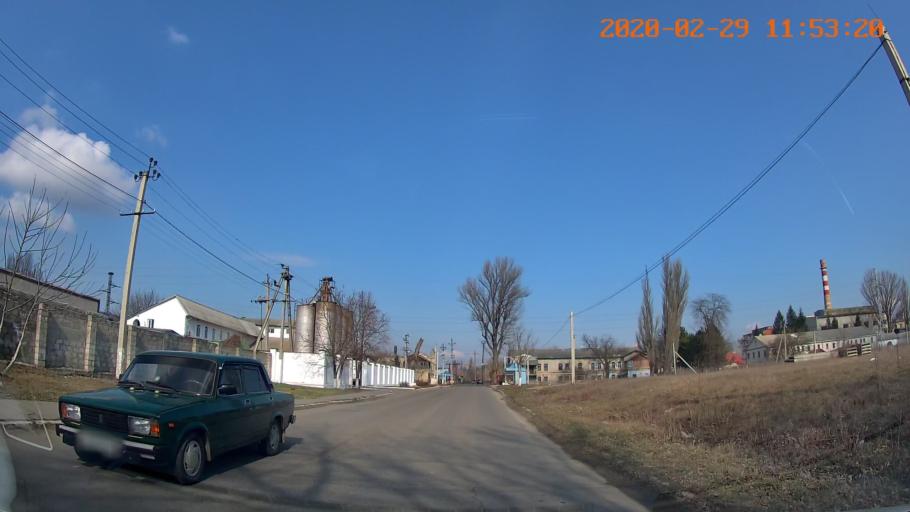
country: MD
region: Telenesti
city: Ribnita
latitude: 47.7765
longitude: 28.9908
